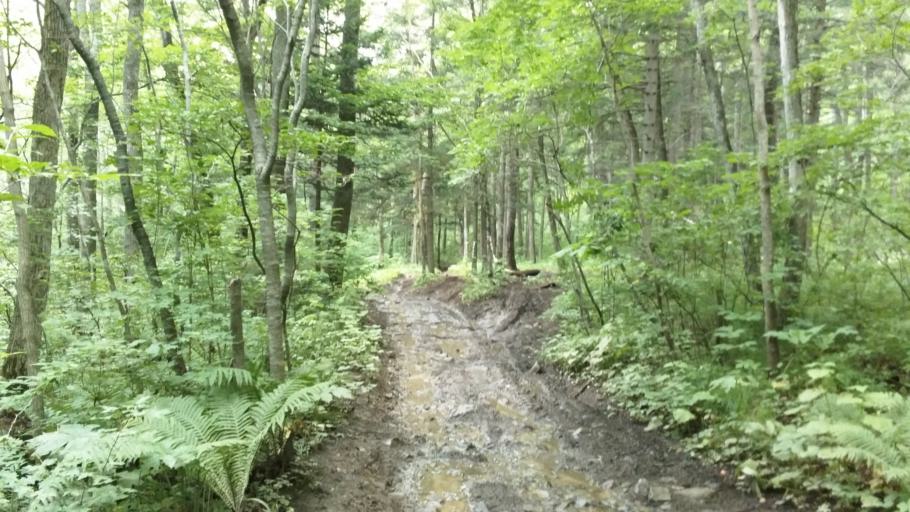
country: RU
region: Primorskiy
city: Trudovoye
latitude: 43.2078
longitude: 132.0029
